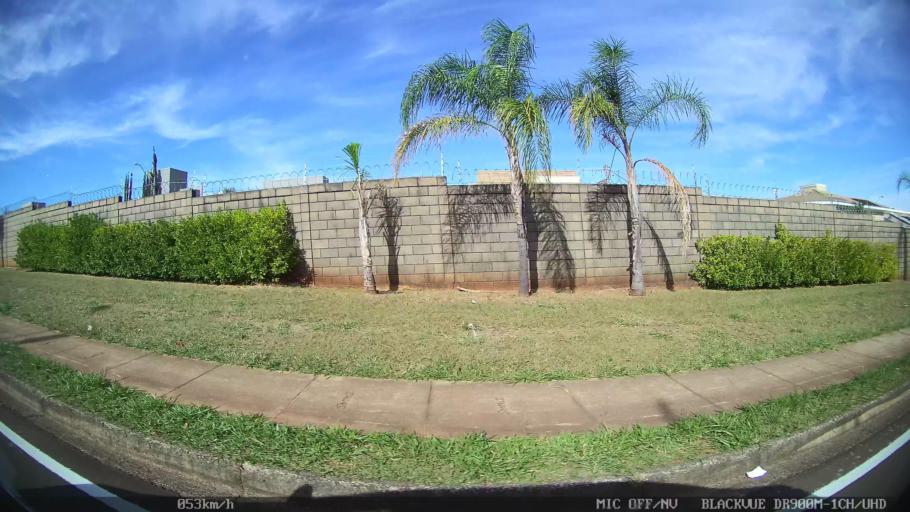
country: BR
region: Sao Paulo
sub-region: Sao Jose Do Rio Preto
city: Sao Jose do Rio Preto
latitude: -20.8096
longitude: -49.3343
